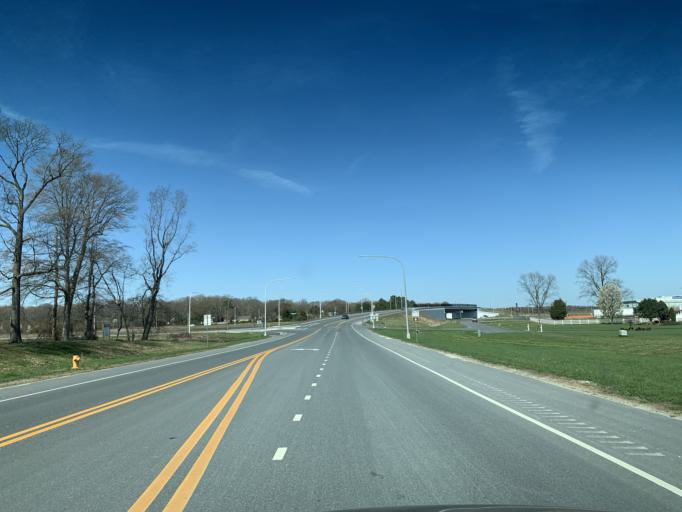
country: US
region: Delaware
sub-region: Sussex County
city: Milford
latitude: 38.9234
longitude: -75.4153
